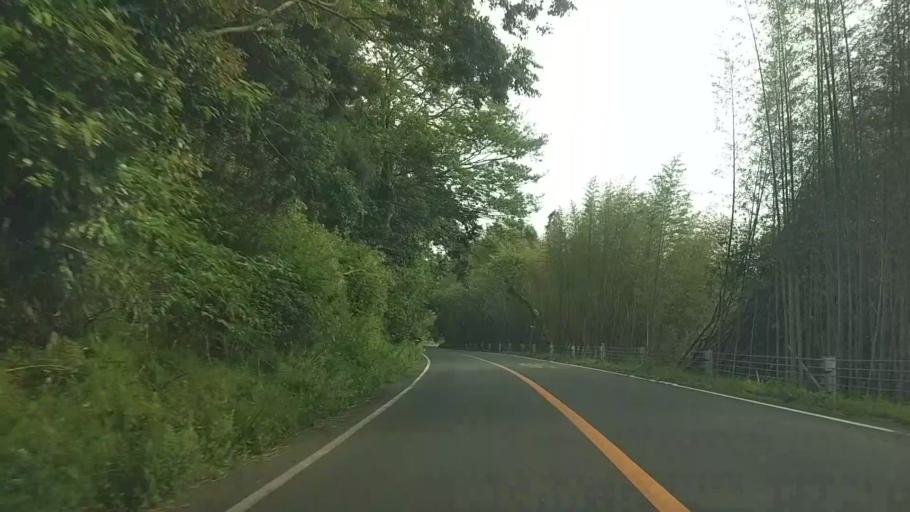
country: JP
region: Shizuoka
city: Kosai-shi
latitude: 34.7473
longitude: 137.5991
